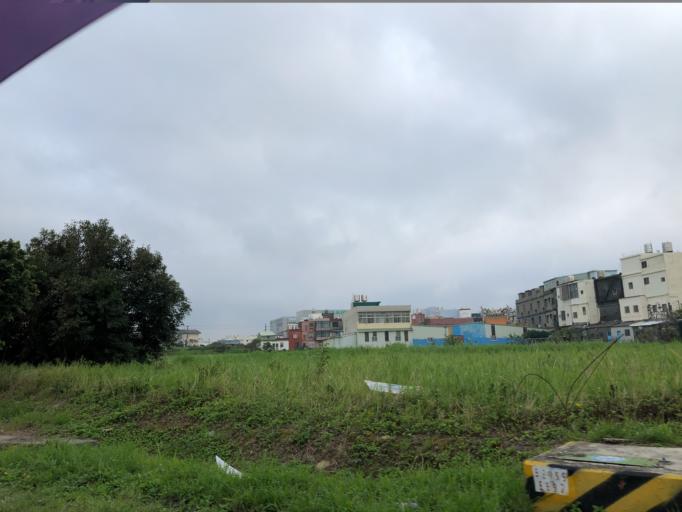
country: TW
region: Taiwan
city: Taoyuan City
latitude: 25.1077
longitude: 121.2430
